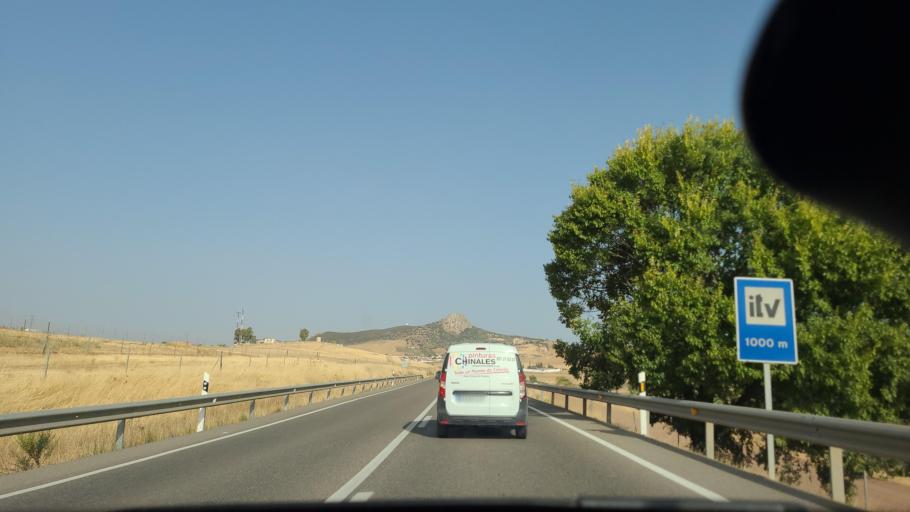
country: ES
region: Andalusia
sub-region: Province of Cordoba
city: Penarroya-Pueblonuevo
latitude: 38.3062
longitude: -5.2592
